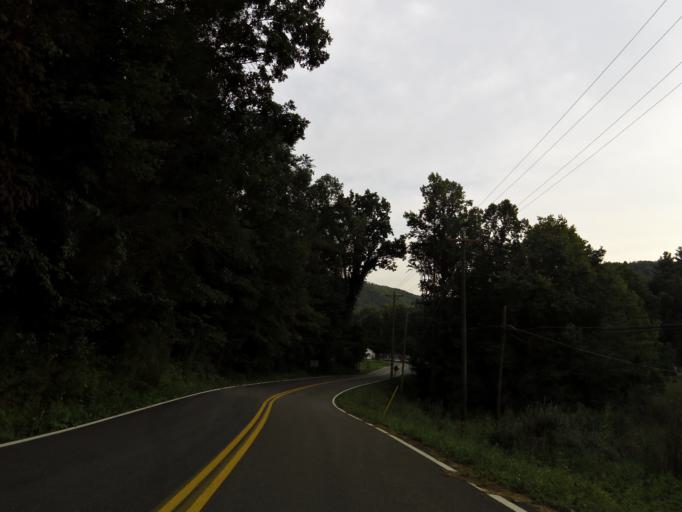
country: US
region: Tennessee
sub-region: Anderson County
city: Clinton
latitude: 36.1207
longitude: -84.2350
